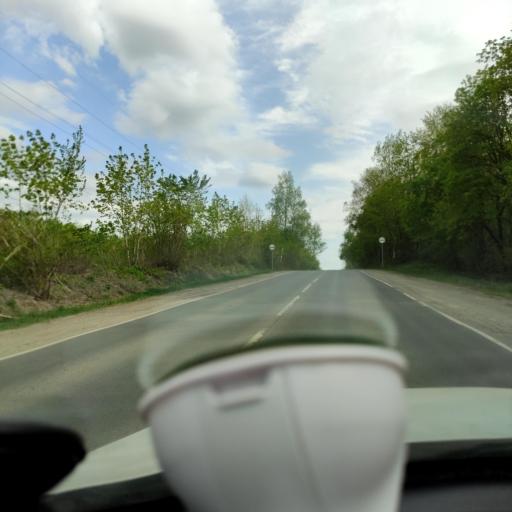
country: RU
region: Samara
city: Novosemeykino
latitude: 53.3420
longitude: 50.2469
